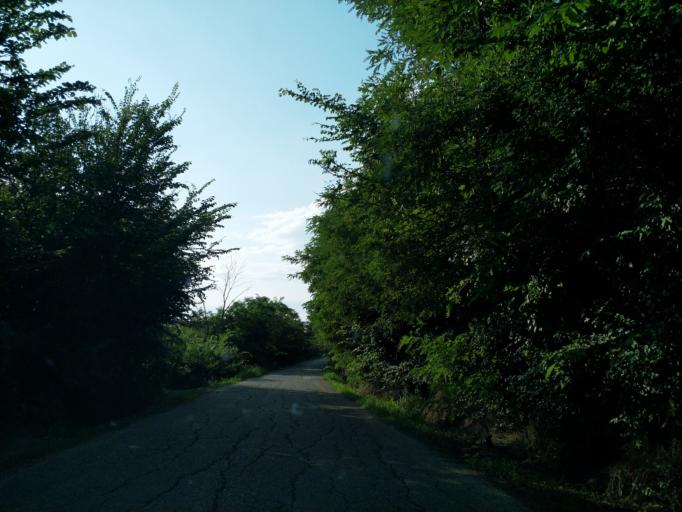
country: RS
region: Central Serbia
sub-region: Pomoravski Okrug
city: Jagodina
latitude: 43.9955
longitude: 21.1946
